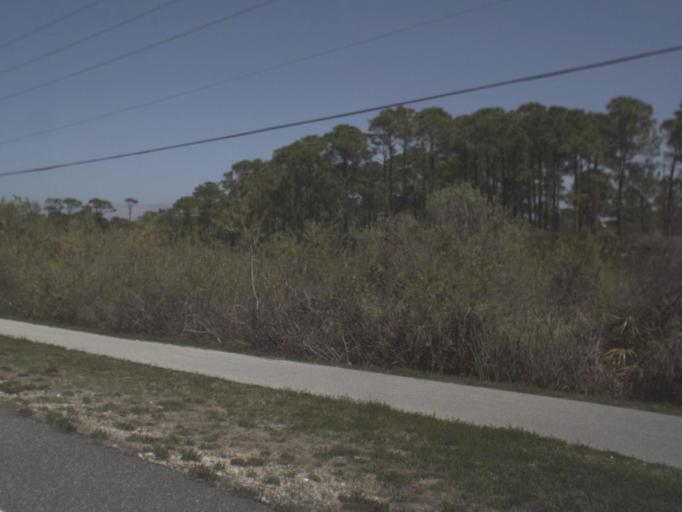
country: US
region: Florida
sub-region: Gulf County
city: Port Saint Joe
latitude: 29.7400
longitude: -85.3944
